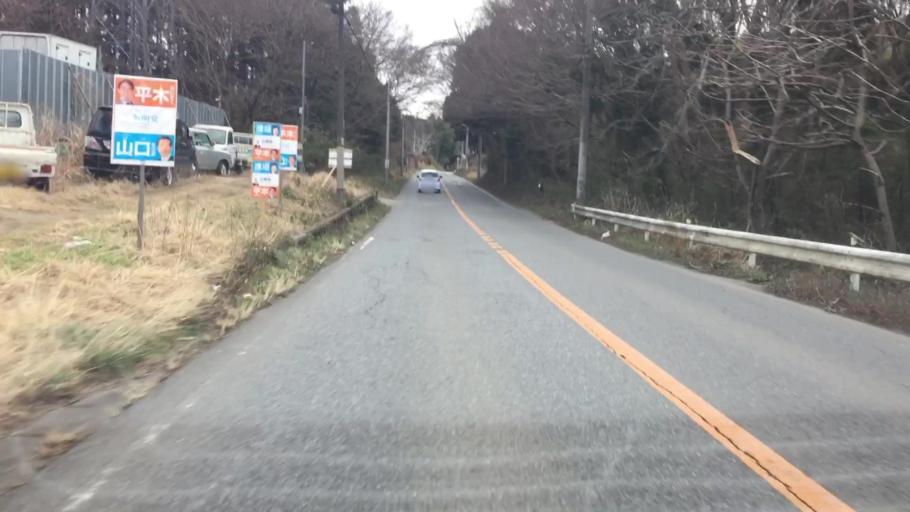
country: JP
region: Ibaraki
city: Ryugasaki
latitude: 35.8224
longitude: 140.1705
